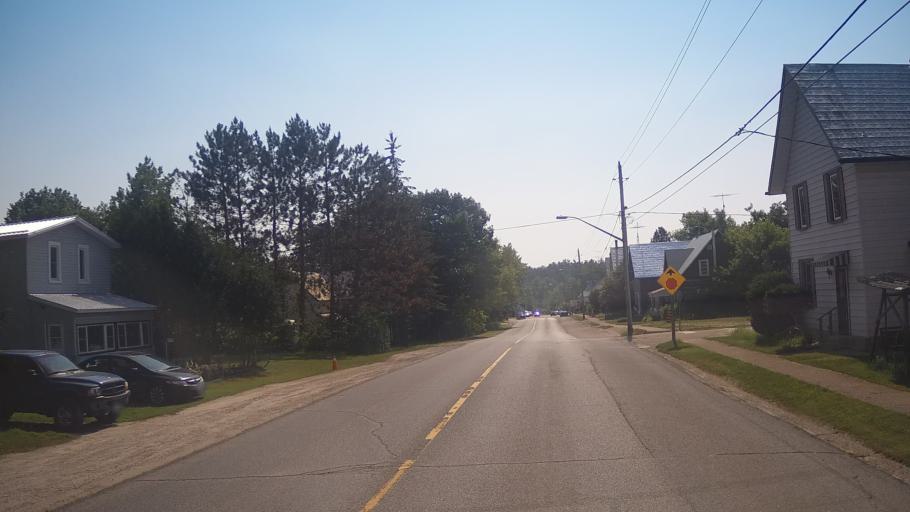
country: CA
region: Ontario
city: Pembroke
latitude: 45.5817
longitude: -77.2416
